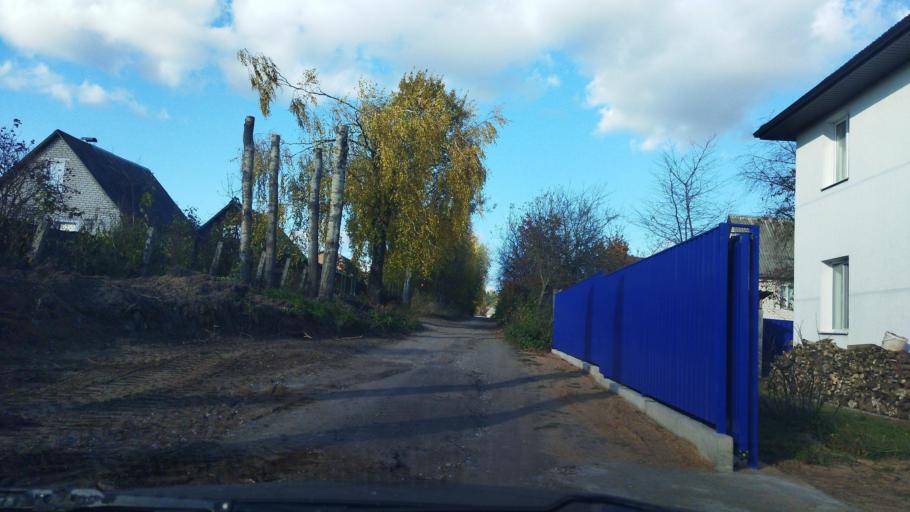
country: BY
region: Minsk
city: Slabada
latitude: 53.9867
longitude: 27.8995
